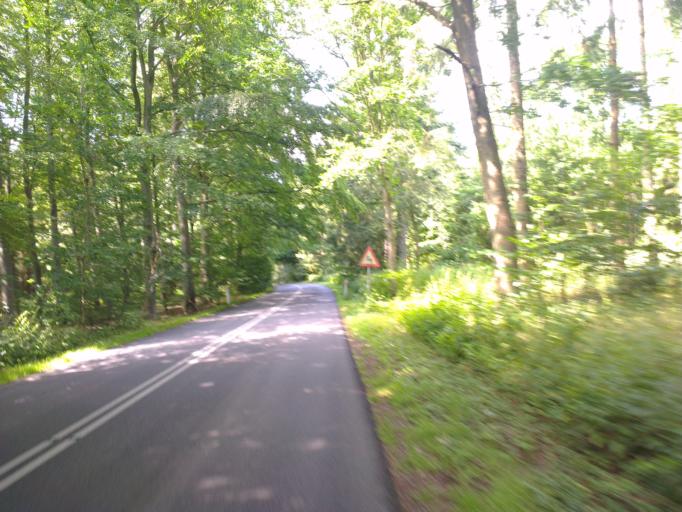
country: DK
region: Zealand
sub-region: Lejre Kommune
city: Ejby
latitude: 55.7347
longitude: 11.8835
